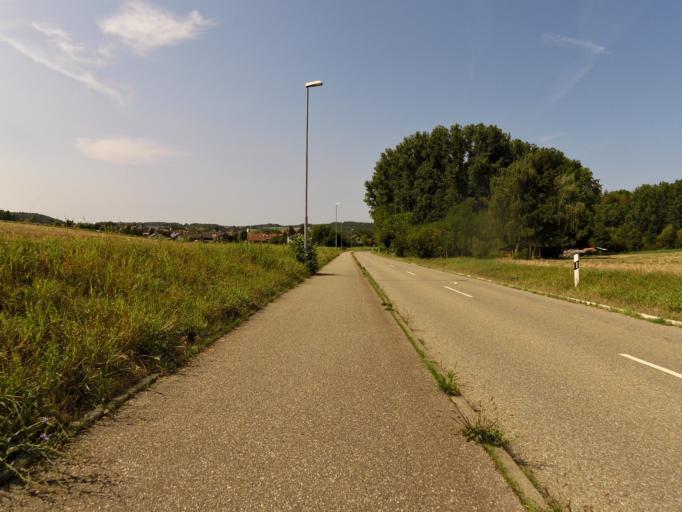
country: DE
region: Baden-Wuerttemberg
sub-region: Karlsruhe Region
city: Neidenstein
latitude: 49.3181
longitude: 8.8777
